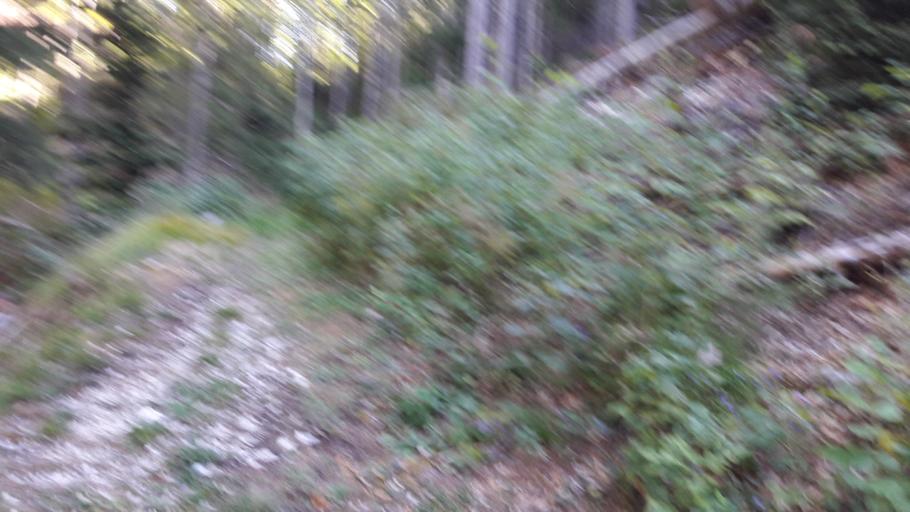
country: CH
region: Solothurn
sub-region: Bezirk Thal
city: Laupersdorf
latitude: 47.3287
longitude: 7.6527
